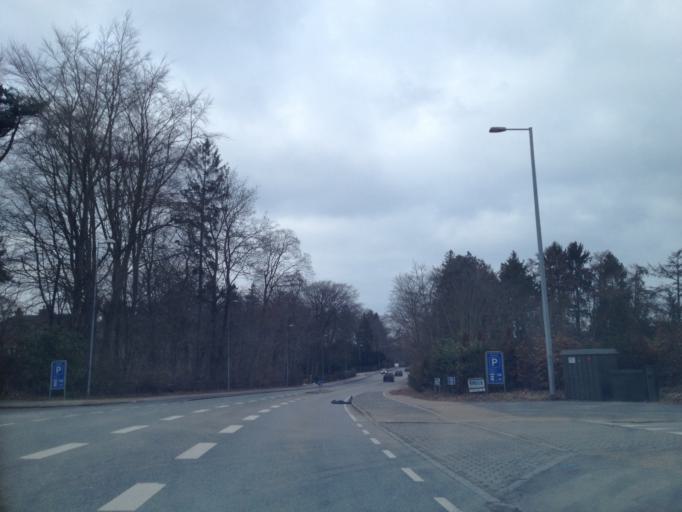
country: DK
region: Capital Region
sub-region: Rudersdal Kommune
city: Trorod
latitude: 55.8677
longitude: 12.5505
